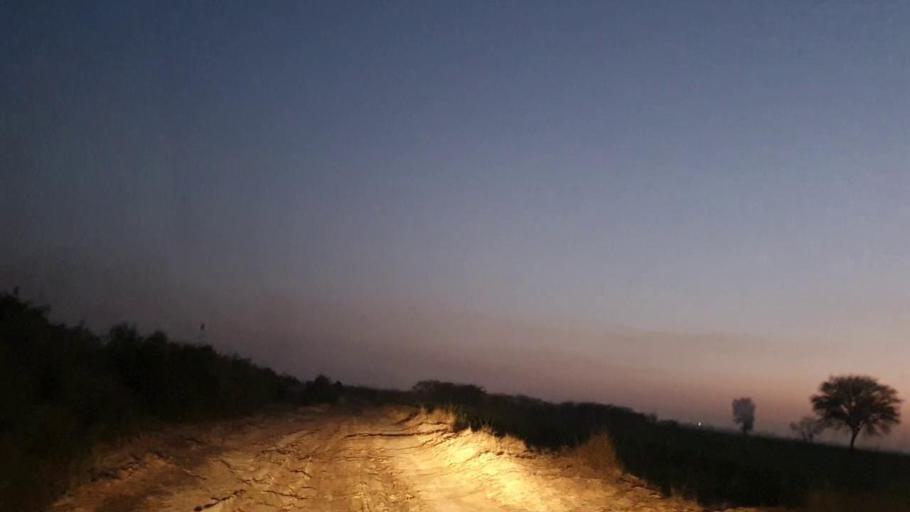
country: PK
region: Sindh
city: Nawabshah
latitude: 26.3253
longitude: 68.3774
